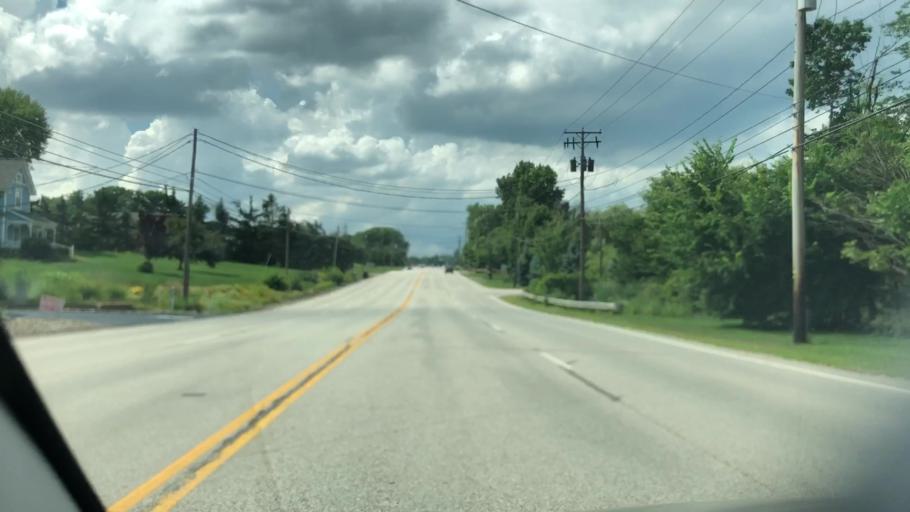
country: US
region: Ohio
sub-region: Summit County
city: Montrose-Ghent
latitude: 41.1462
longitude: -81.6236
